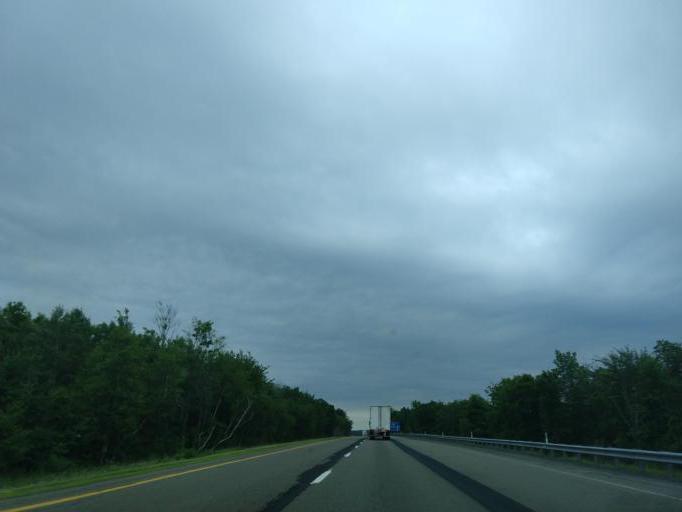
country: US
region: Pennsylvania
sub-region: Schuylkill County
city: Mahanoy City
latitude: 40.8179
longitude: -76.0919
